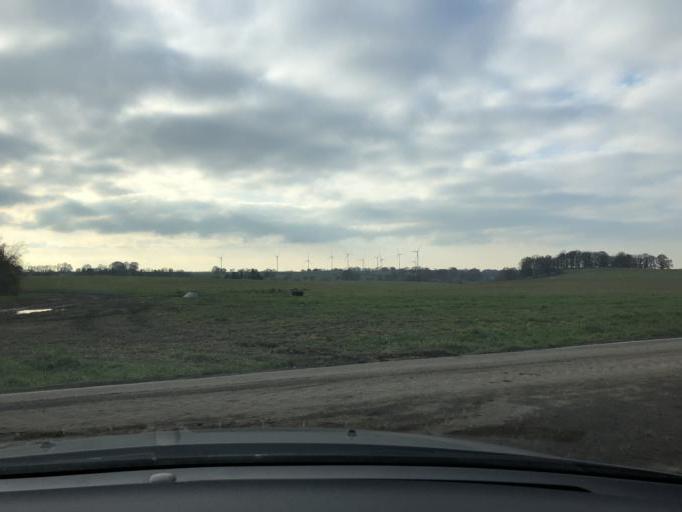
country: DE
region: Saxony
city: Mutzschen
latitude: 51.2704
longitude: 12.8899
